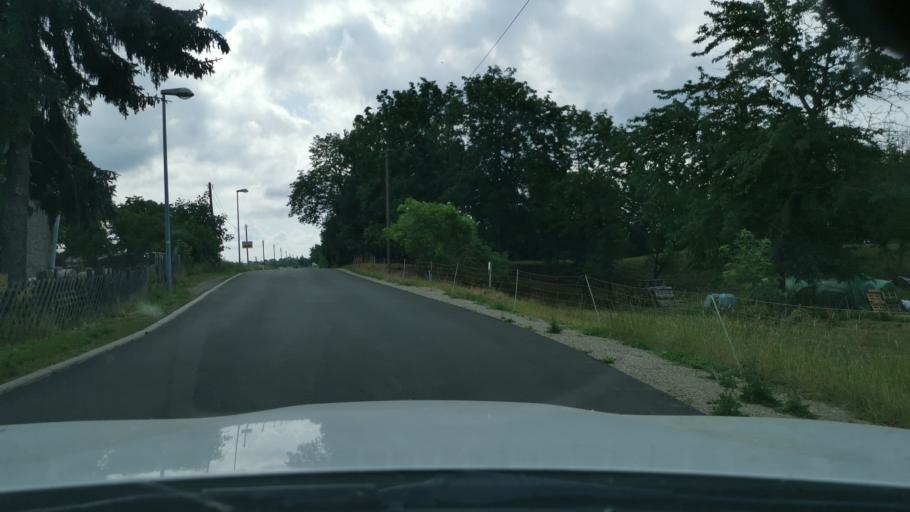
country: DE
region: Saxony
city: Torgau
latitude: 51.6050
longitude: 13.0264
